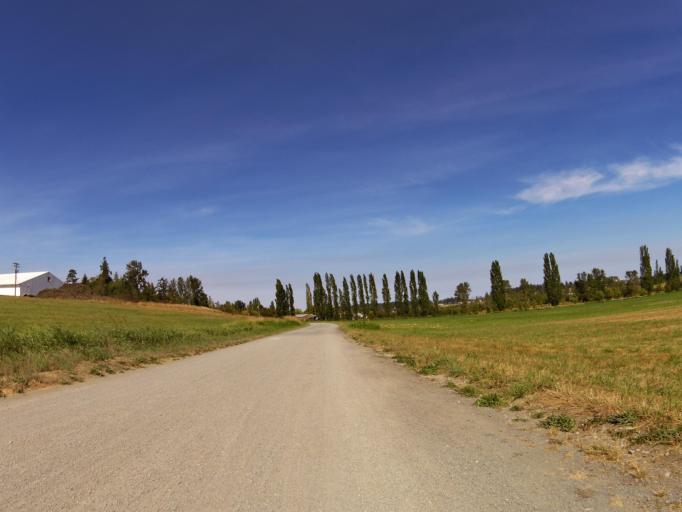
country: CA
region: British Columbia
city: North Saanich
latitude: 48.5557
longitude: -123.3864
